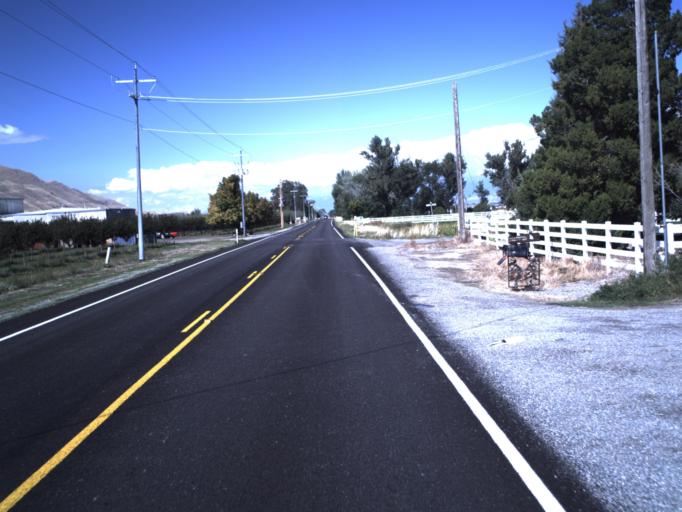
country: US
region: Utah
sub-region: Utah County
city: West Mountain
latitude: 40.0310
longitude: -111.7871
